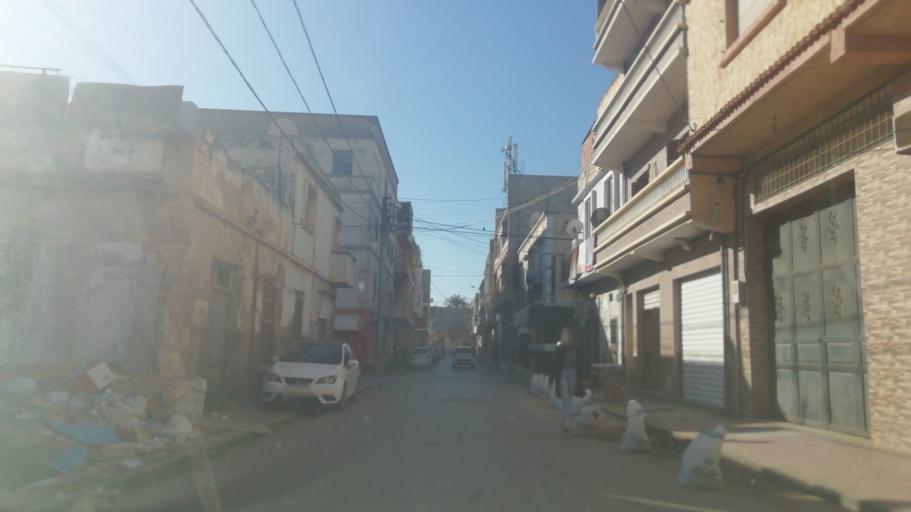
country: DZ
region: Oran
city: Oran
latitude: 35.6825
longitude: -0.6538
